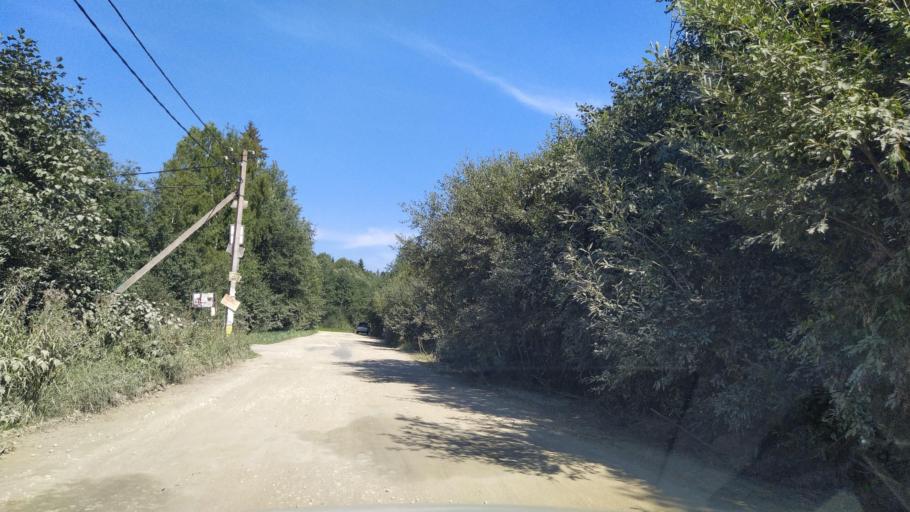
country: RU
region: Leningrad
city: Siverskiy
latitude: 59.2897
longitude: 30.0312
